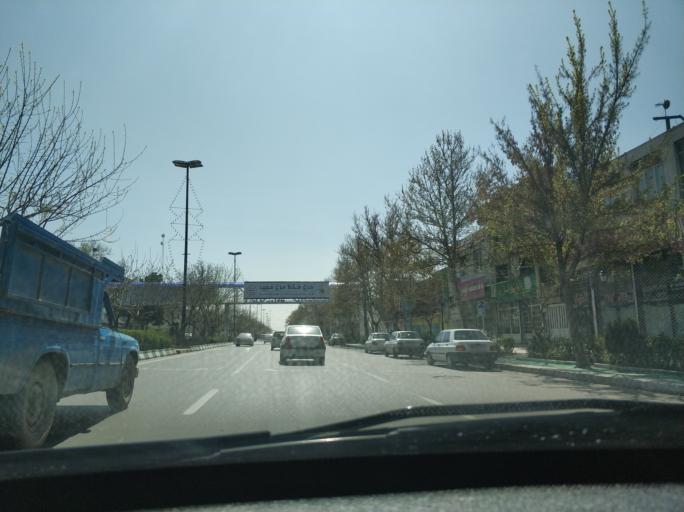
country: IR
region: Razavi Khorasan
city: Mashhad
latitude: 36.2611
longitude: 59.6056
